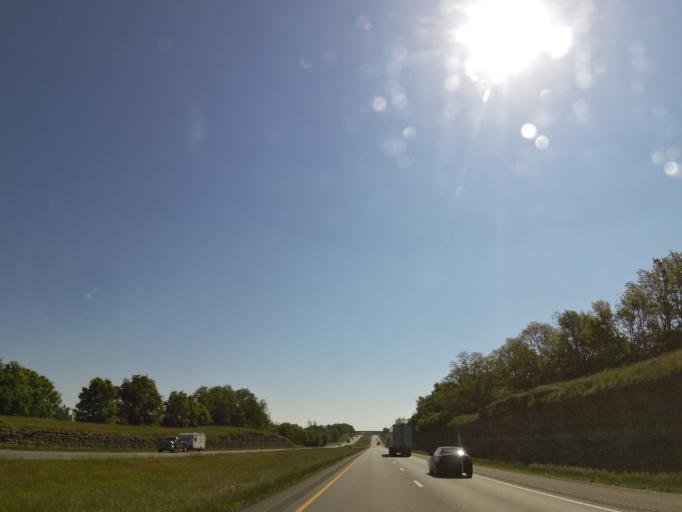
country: US
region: Kentucky
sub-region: Woodford County
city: Midway
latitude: 38.1603
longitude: -84.6483
